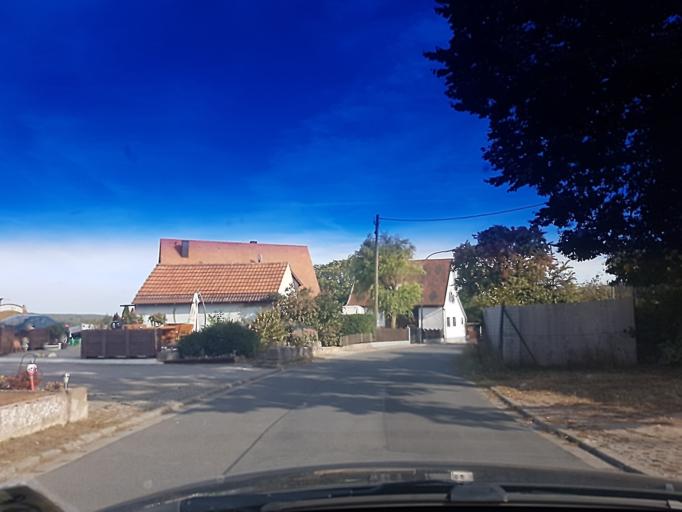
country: DE
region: Bavaria
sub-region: Regierungsbezirk Mittelfranken
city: Burghaslach
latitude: 49.7756
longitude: 10.5450
